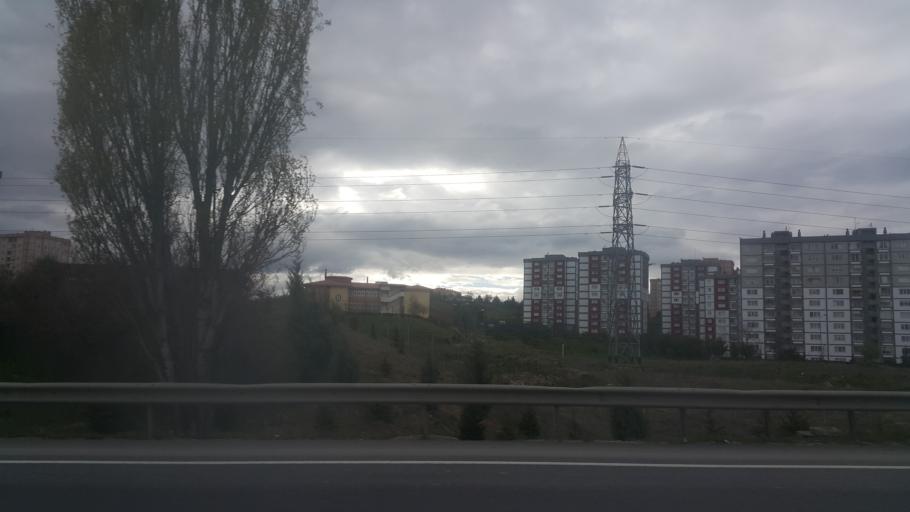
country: TR
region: Ankara
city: Etimesgut
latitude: 39.9739
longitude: 32.6343
